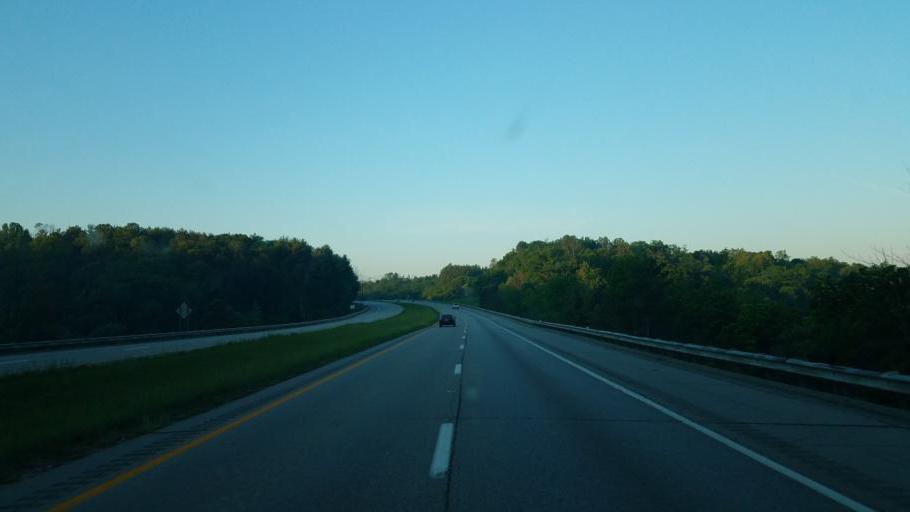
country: US
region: Ohio
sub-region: Washington County
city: Devola
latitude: 39.4604
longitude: -81.4384
